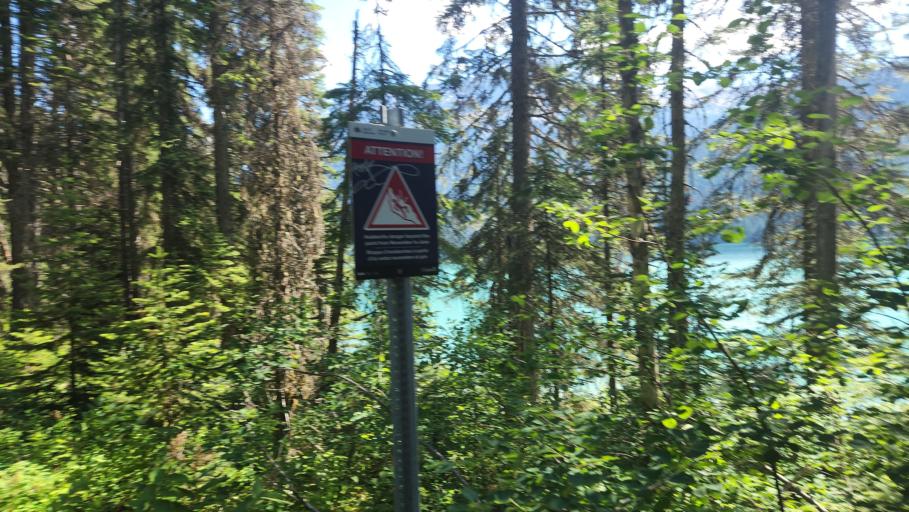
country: CA
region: Alberta
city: Lake Louise
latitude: 51.4420
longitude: -116.5426
